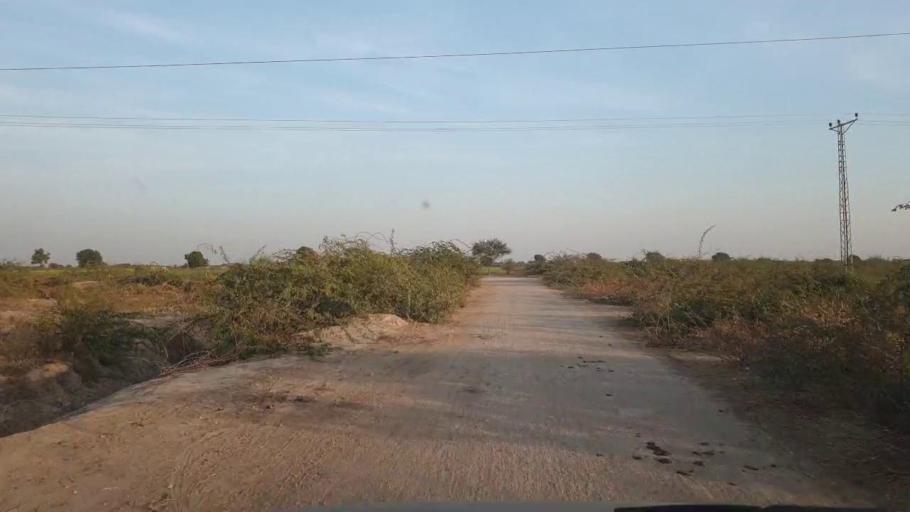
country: PK
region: Sindh
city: Chambar
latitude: 25.2830
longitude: 68.8232
